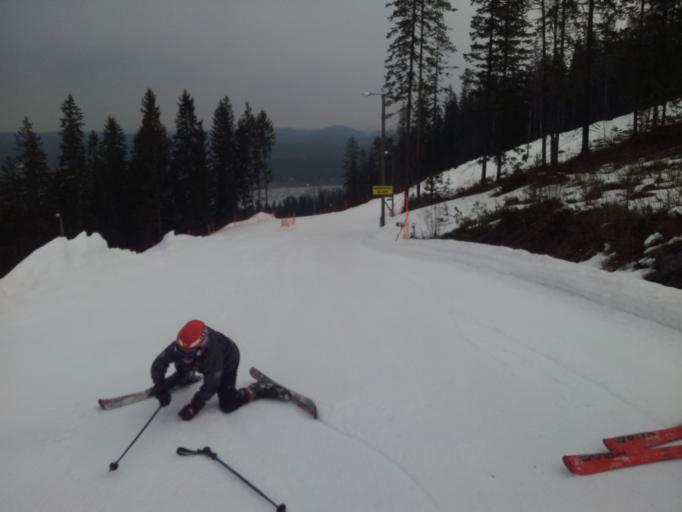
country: FI
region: Central Finland
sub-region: Jaemsae
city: Jaemsae
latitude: 61.8840
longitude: 25.3153
